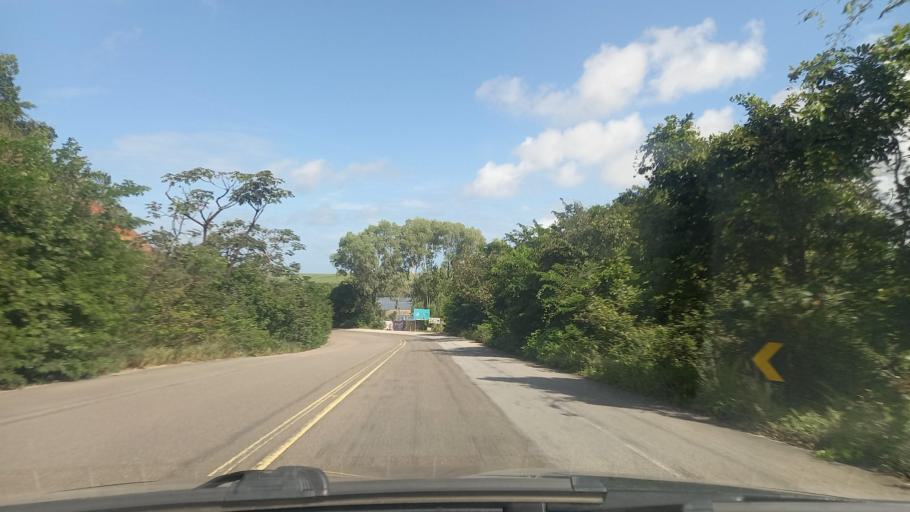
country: BR
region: Alagoas
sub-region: Marechal Deodoro
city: Marechal Deodoro
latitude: -9.8348
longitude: -35.9293
